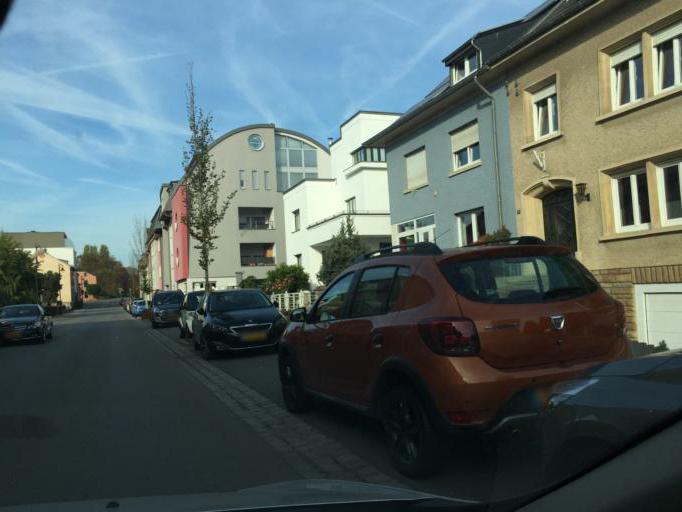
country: LU
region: Diekirch
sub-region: Canton de Diekirch
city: Diekirch
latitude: 49.8659
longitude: 6.1649
